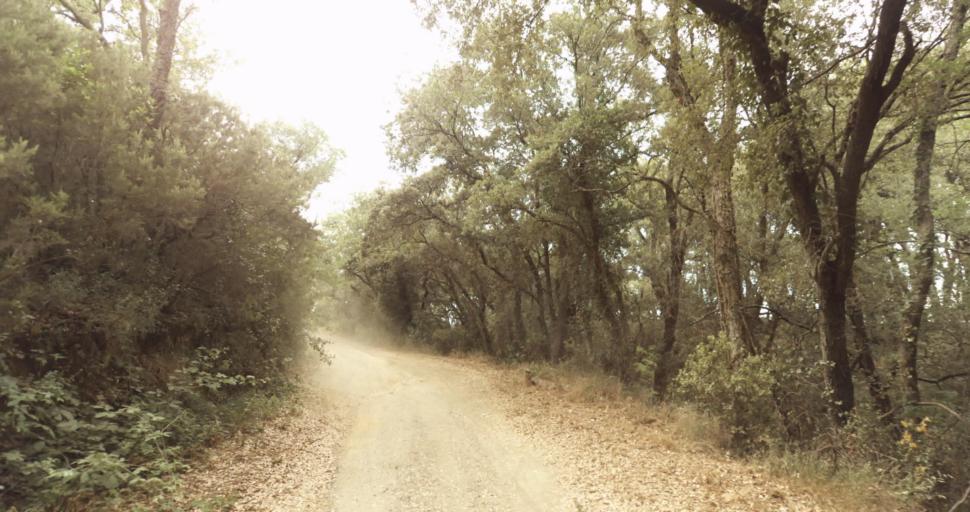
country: FR
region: Provence-Alpes-Cote d'Azur
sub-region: Departement du Var
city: La Croix-Valmer
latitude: 43.2182
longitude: 6.5740
